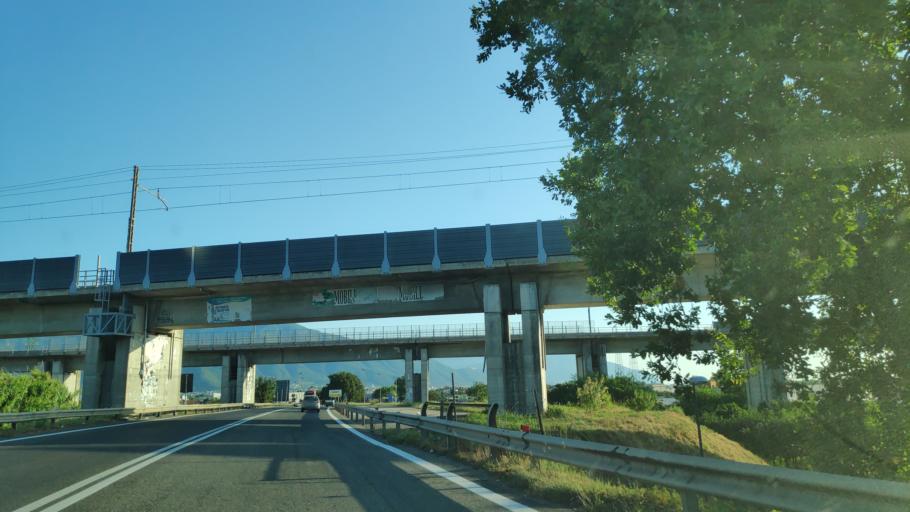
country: IT
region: Campania
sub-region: Provincia di Salerno
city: San Valentino Torio
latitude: 40.7770
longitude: 14.6157
